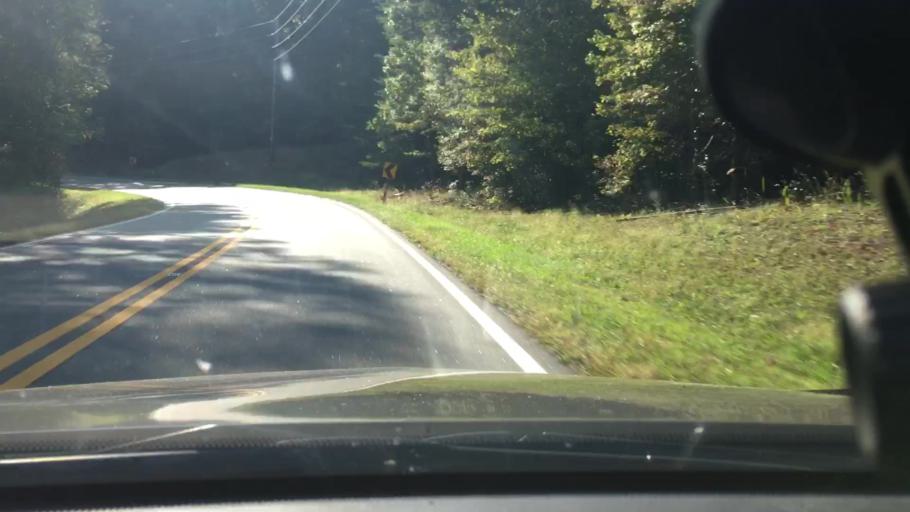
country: US
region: North Carolina
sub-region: Rutherford County
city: Rutherfordton
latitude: 35.3293
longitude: -82.0616
